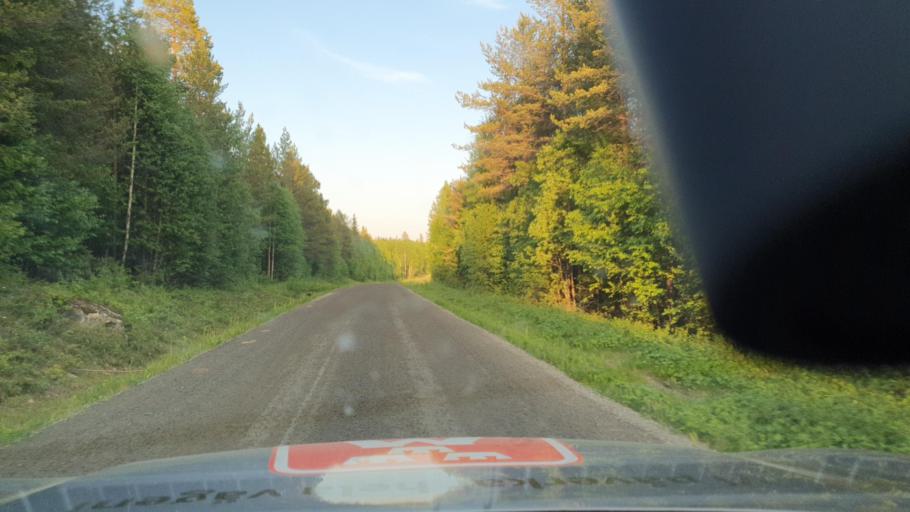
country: SE
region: Norrbotten
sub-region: Bodens Kommun
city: Boden
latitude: 66.0632
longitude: 21.7274
